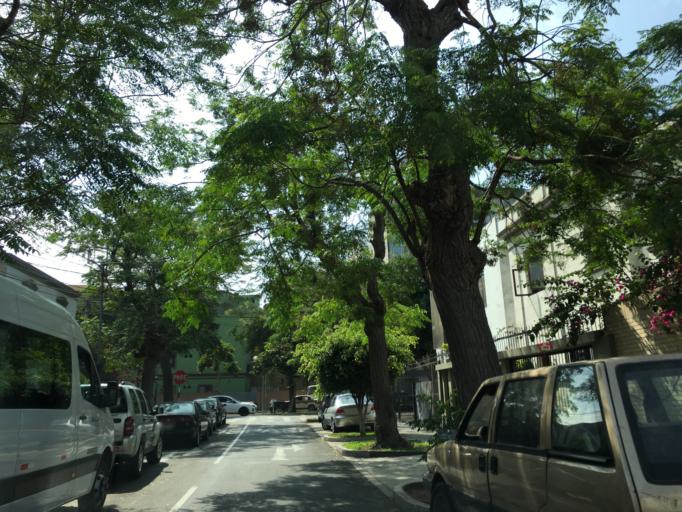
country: PE
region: Lima
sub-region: Lima
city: San Isidro
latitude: -12.1029
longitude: -77.0321
